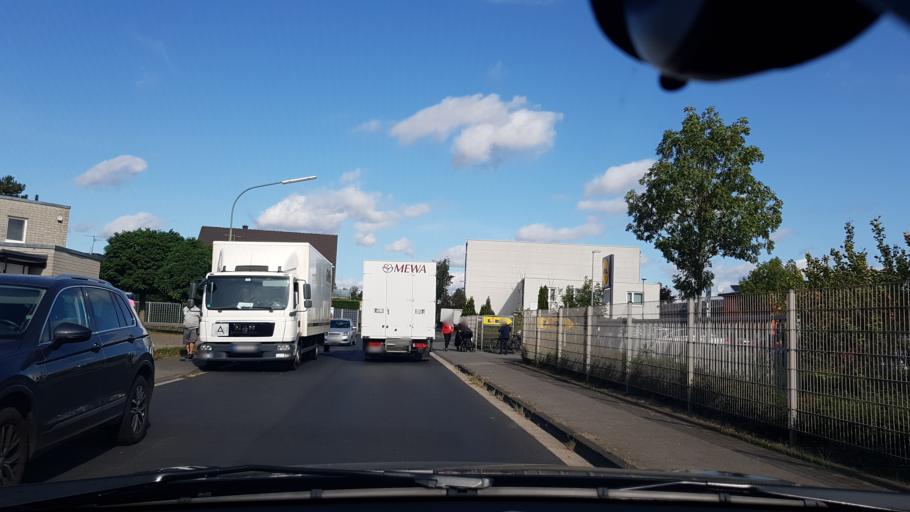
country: DE
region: North Rhine-Westphalia
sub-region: Regierungsbezirk Dusseldorf
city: Neuss
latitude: 51.1475
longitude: 6.7036
